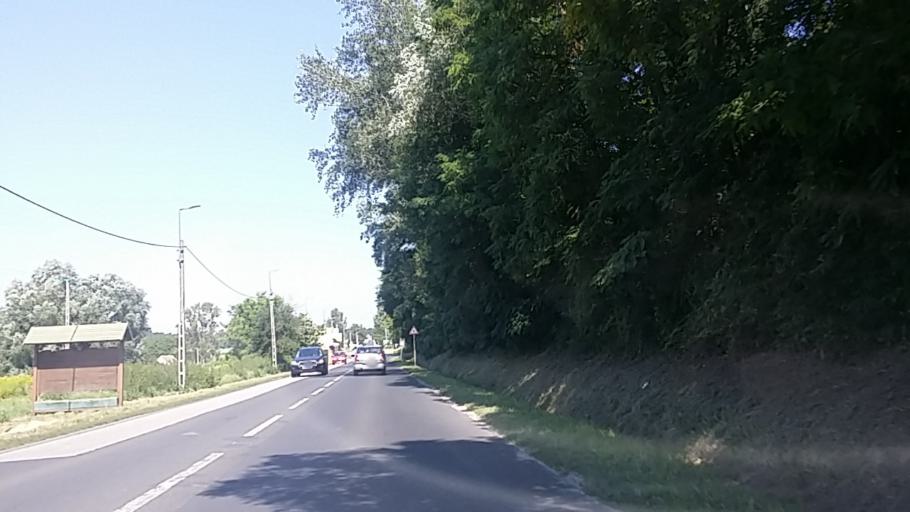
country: HU
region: Zala
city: Cserszegtomaj
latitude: 46.7889
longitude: 17.2129
